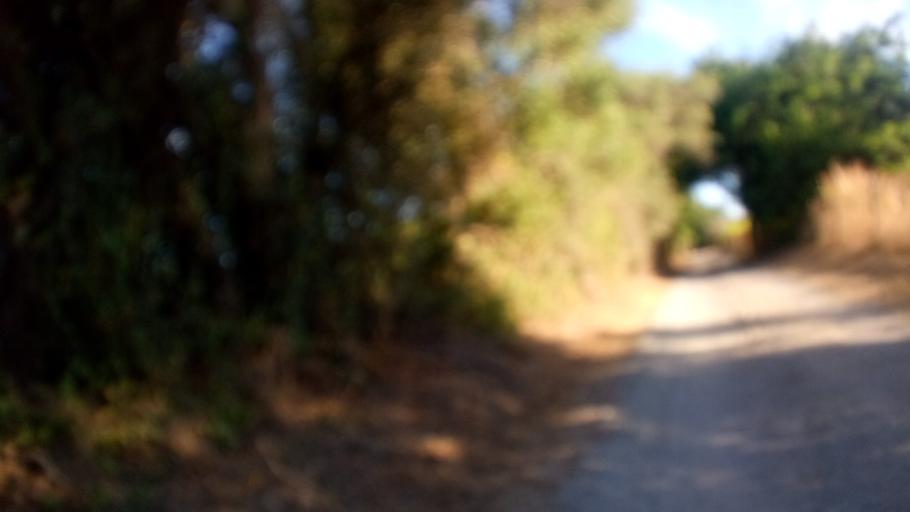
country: PT
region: Faro
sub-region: Tavira
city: Tavira
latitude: 37.1445
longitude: -7.5939
